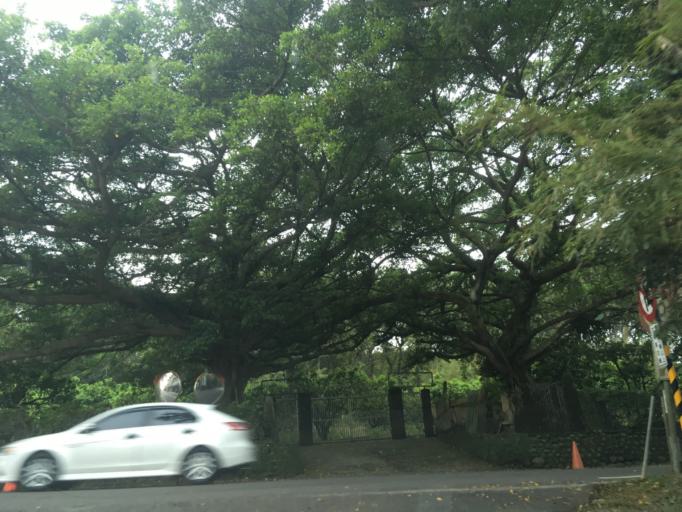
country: TW
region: Taiwan
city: Daxi
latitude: 24.8834
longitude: 121.3002
